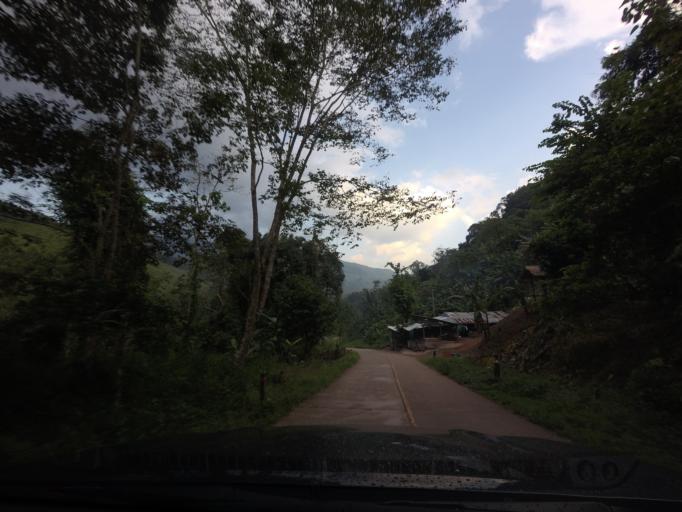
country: TH
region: Nan
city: Bo Kluea
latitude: 19.1943
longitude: 101.1945
